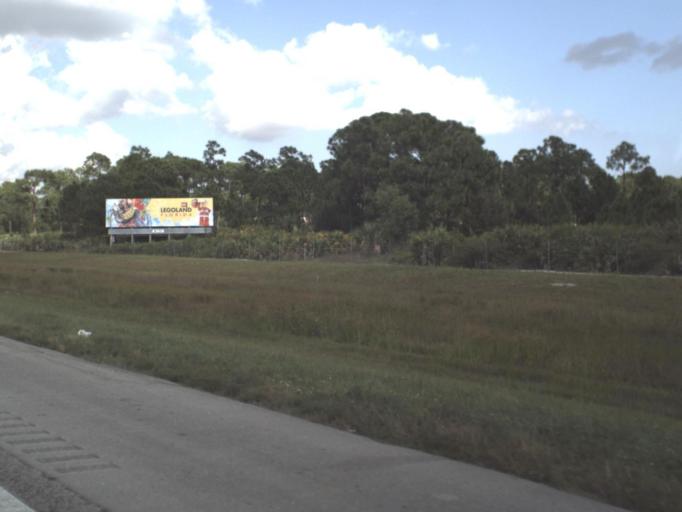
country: US
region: Florida
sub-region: Saint Lucie County
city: Fort Pierce South
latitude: 27.3857
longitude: -80.3894
